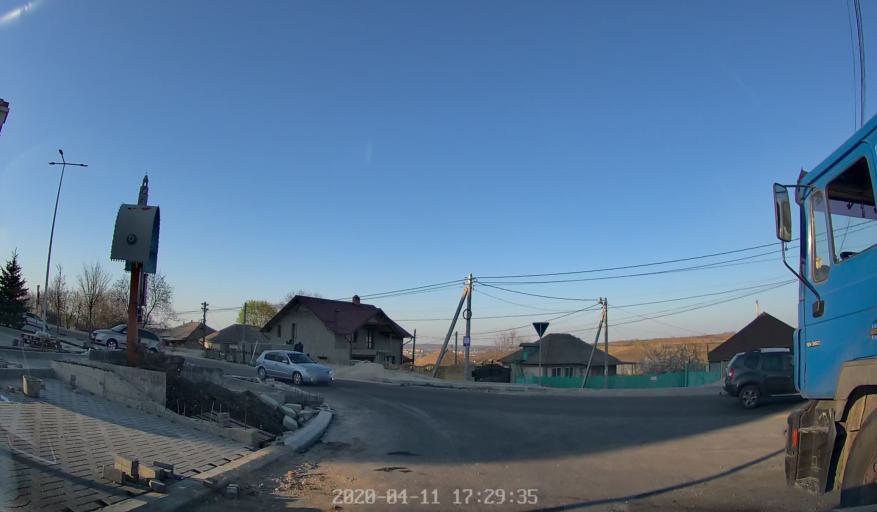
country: MD
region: Laloveni
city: Ialoveni
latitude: 47.0067
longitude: 28.7647
